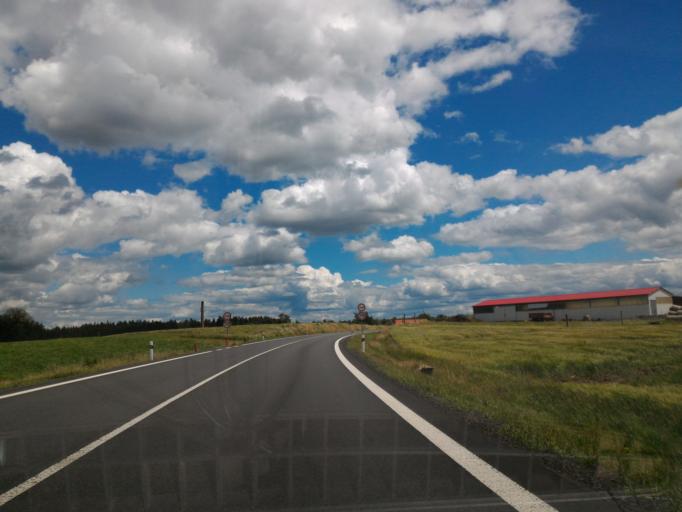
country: CZ
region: Vysocina
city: Bohdalov
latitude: 49.4856
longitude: 15.8706
